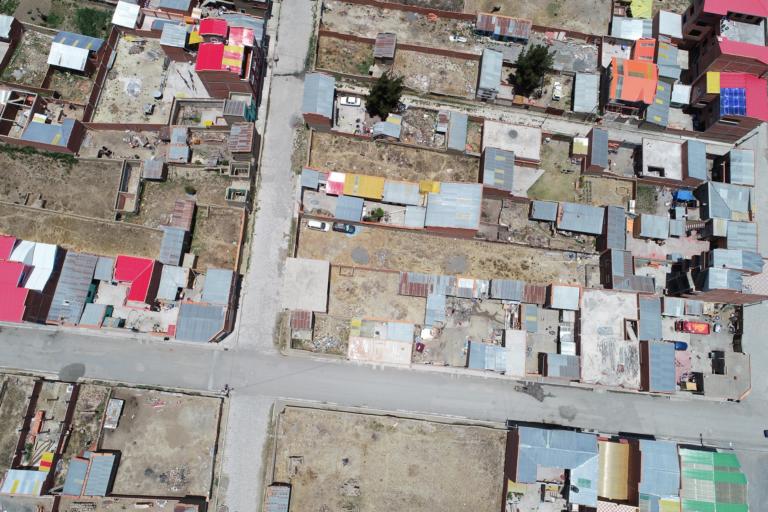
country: BO
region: La Paz
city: Achacachi
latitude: -16.0492
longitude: -68.6854
